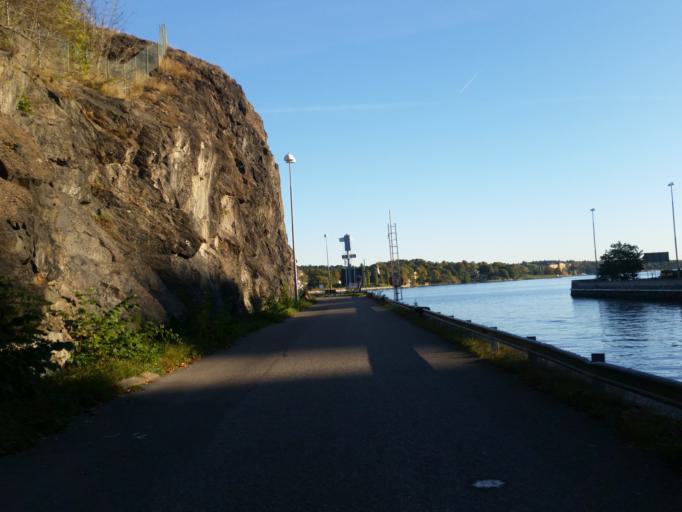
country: SE
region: Stockholm
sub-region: Stockholms Kommun
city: OEstermalm
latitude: 59.3147
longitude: 18.1060
